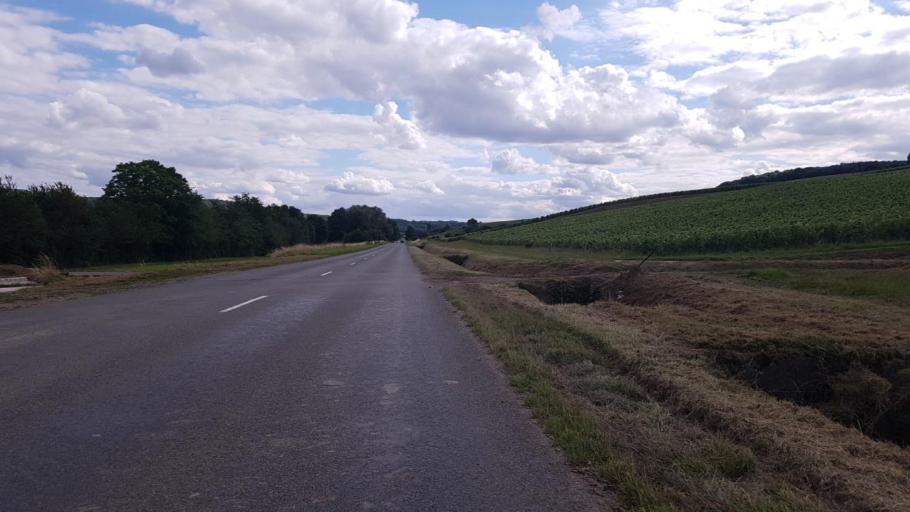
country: FR
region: Picardie
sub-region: Departement de l'Aisne
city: Crezancy
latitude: 49.0649
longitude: 3.4791
